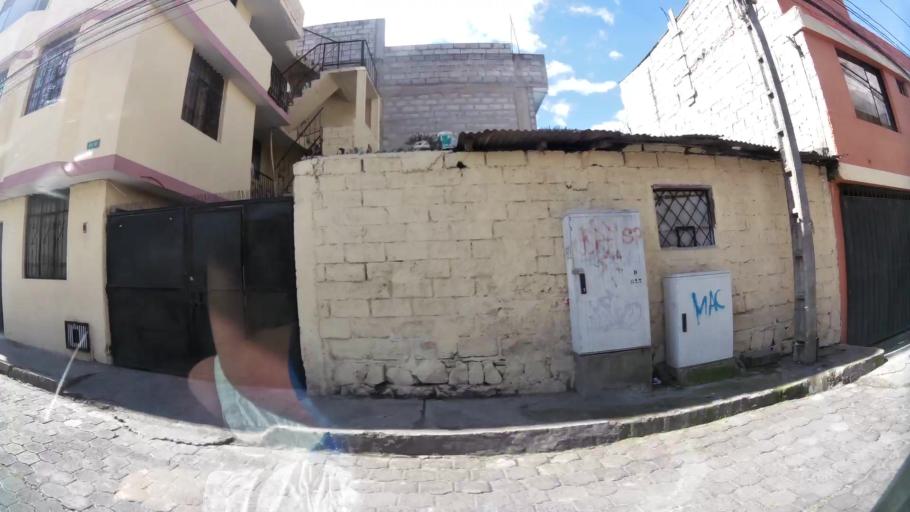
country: EC
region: Pichincha
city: Quito
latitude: -0.1220
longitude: -78.4651
